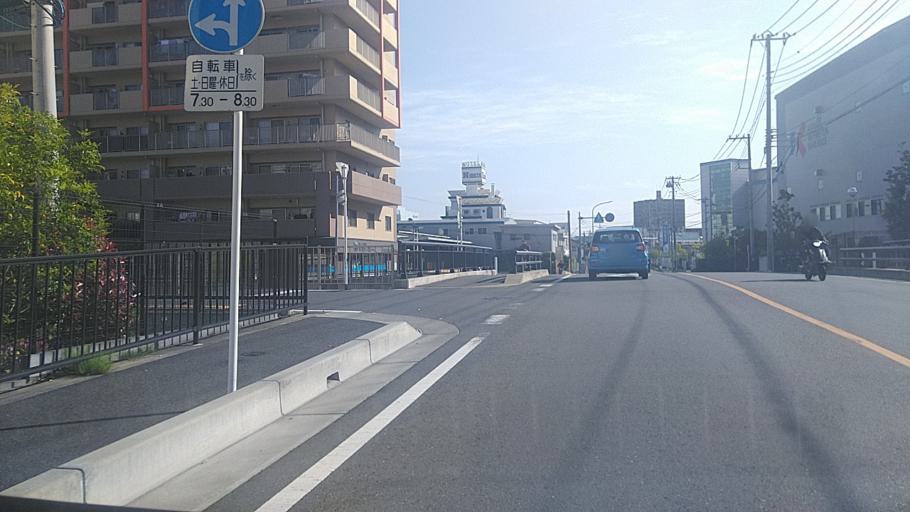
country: JP
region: Saitama
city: Wako
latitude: 35.8065
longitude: 139.6514
